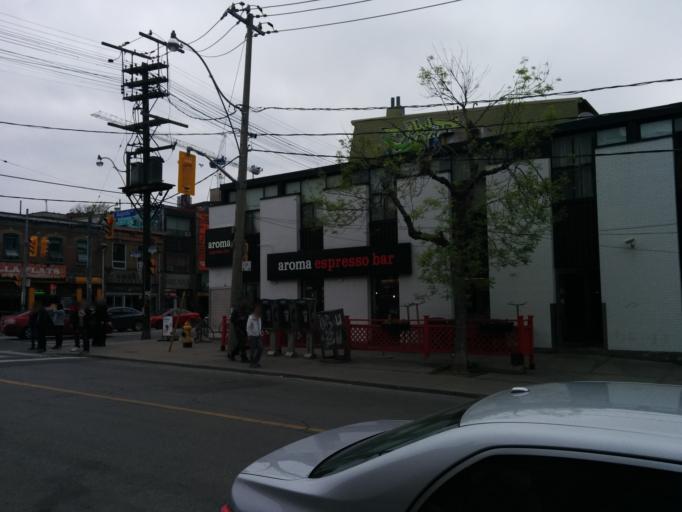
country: CA
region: Ontario
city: Toronto
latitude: 43.6478
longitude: -79.3999
